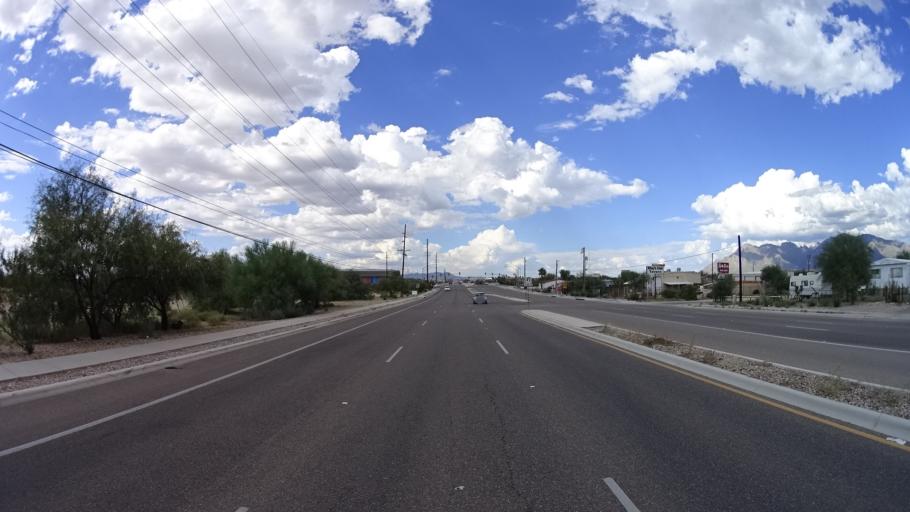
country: US
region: Arizona
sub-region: Pima County
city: Flowing Wells
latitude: 32.2997
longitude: -111.0121
